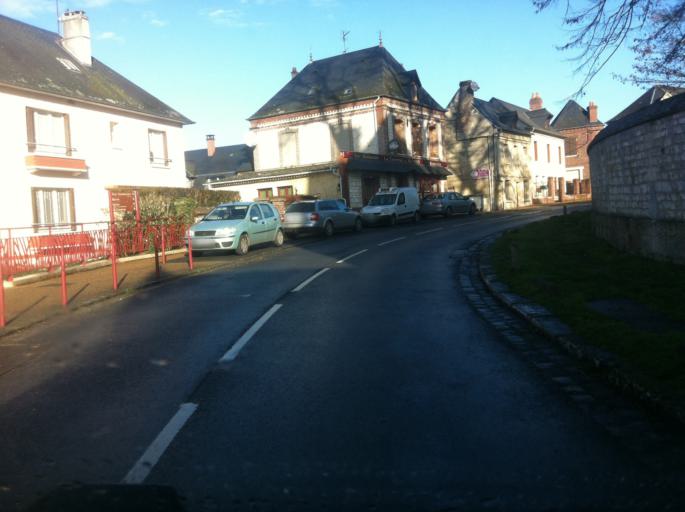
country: FR
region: Haute-Normandie
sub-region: Departement de la Seine-Maritime
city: Jumieges
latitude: 49.4317
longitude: 0.8180
